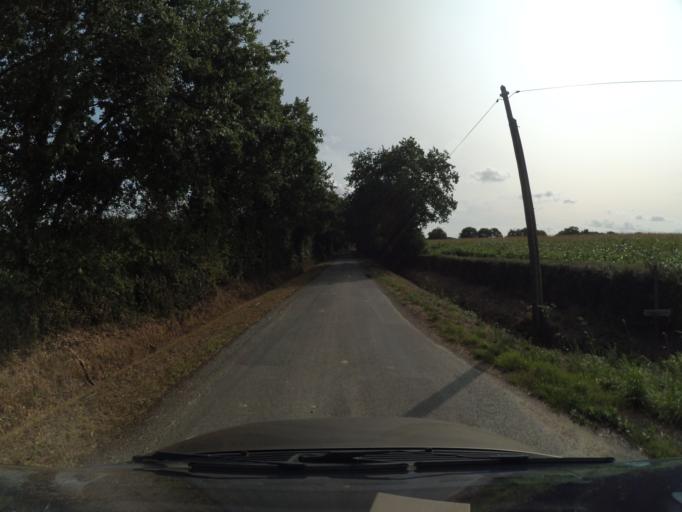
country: FR
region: Pays de la Loire
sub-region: Departement de la Vendee
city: Bouffere
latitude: 46.9426
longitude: -1.3288
